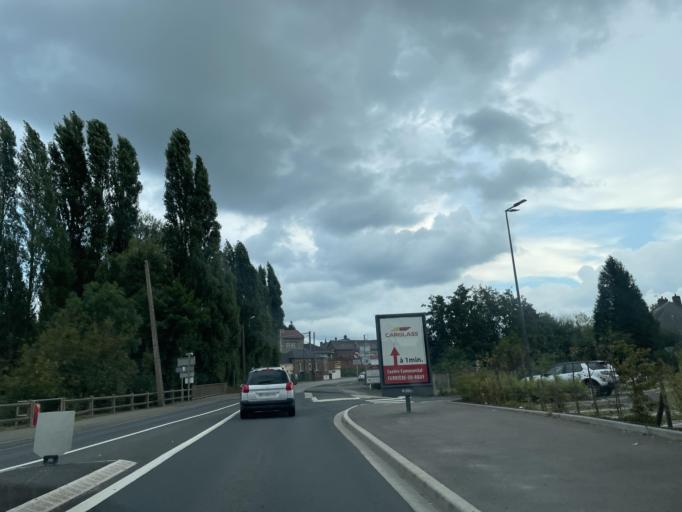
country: FR
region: Haute-Normandie
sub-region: Departement de la Seine-Maritime
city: Gournay-en-Bray
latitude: 49.4844
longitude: 1.7326
